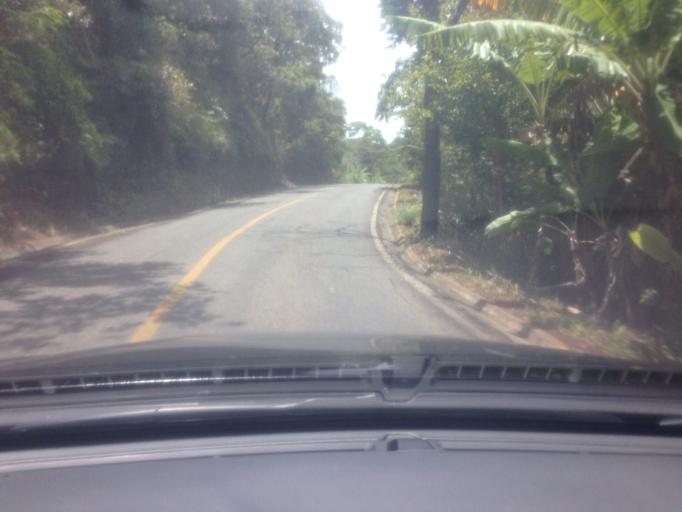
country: BR
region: Espirito Santo
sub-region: Guarapari
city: Guarapari
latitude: -20.5927
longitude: -40.5392
